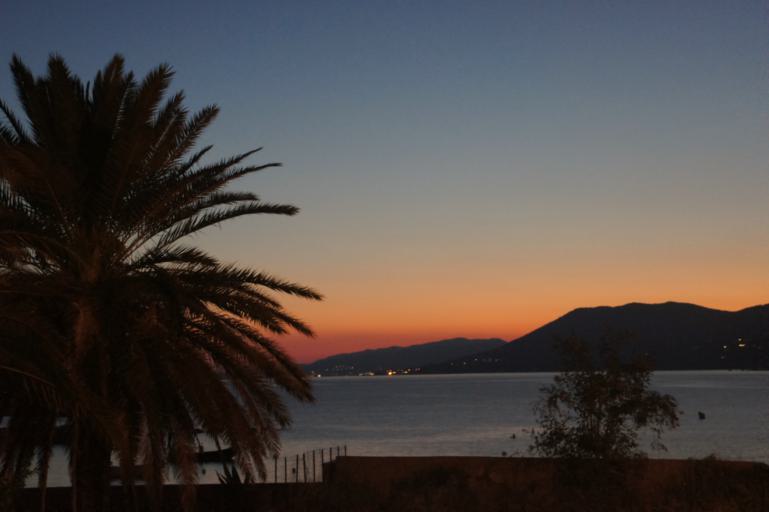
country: FR
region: Corsica
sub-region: Departement de la Corse-du-Sud
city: Propriano
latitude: 41.6775
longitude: 8.9100
